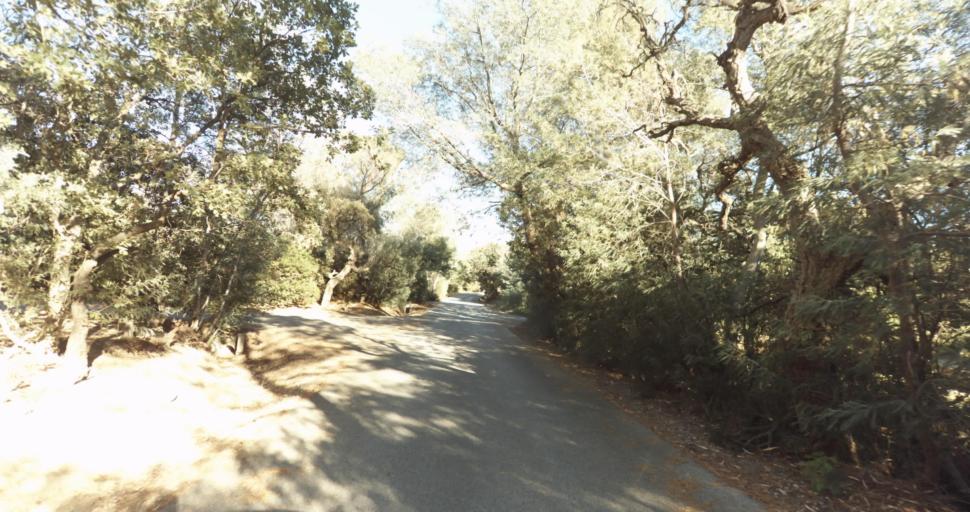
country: FR
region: Provence-Alpes-Cote d'Azur
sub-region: Departement du Var
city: Gassin
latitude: 43.2351
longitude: 6.5995
